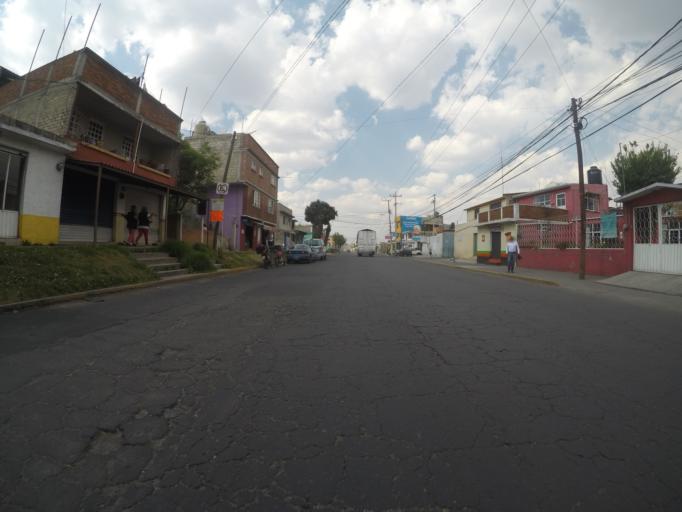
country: MX
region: Mexico
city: San Buenaventura
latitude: 19.2576
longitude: -99.6599
